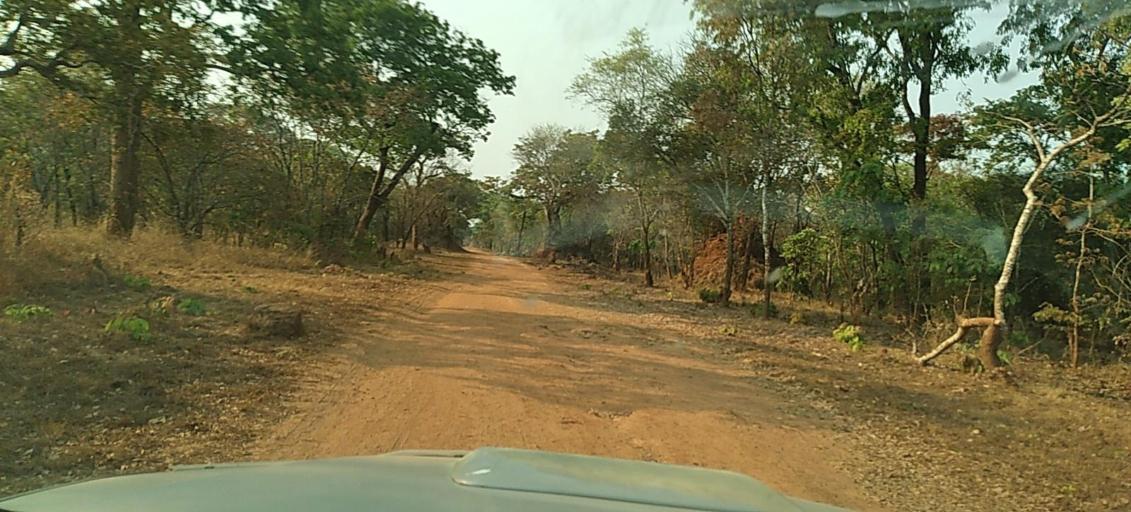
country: ZM
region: North-Western
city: Kasempa
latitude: -13.2908
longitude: 26.5553
